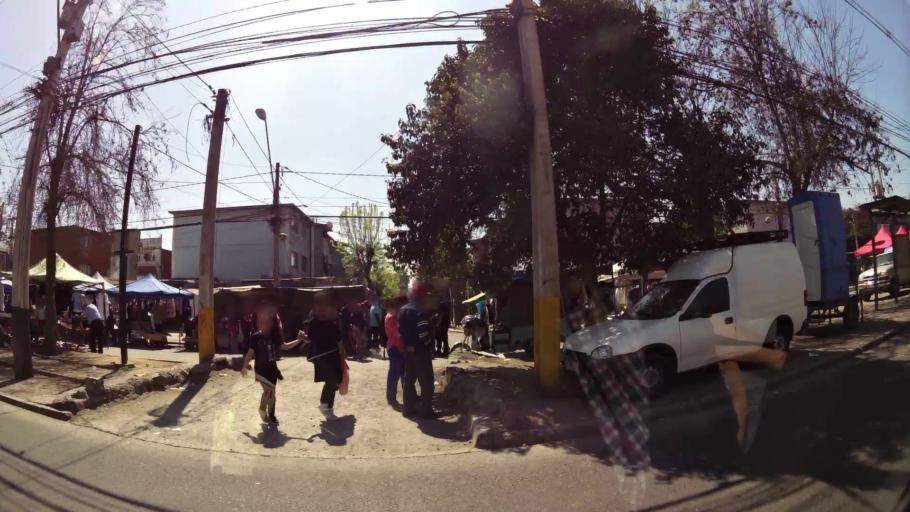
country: CL
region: Santiago Metropolitan
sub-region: Provincia de Santiago
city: Lo Prado
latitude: -33.3656
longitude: -70.7448
